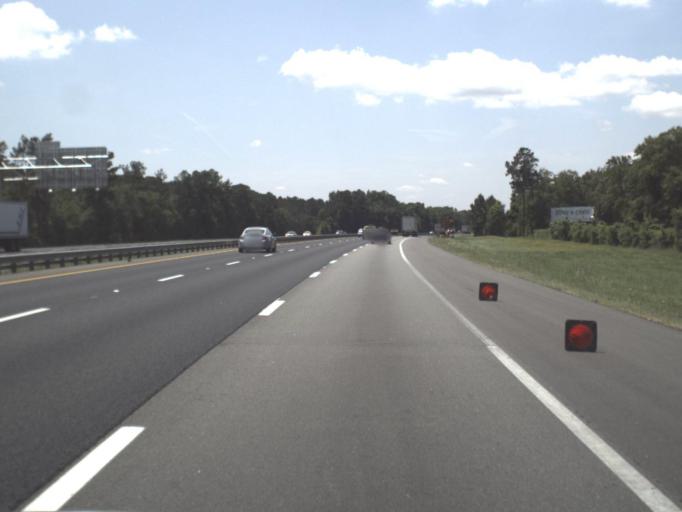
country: US
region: Florida
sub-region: Nassau County
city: Yulee
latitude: 30.6033
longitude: -81.6449
